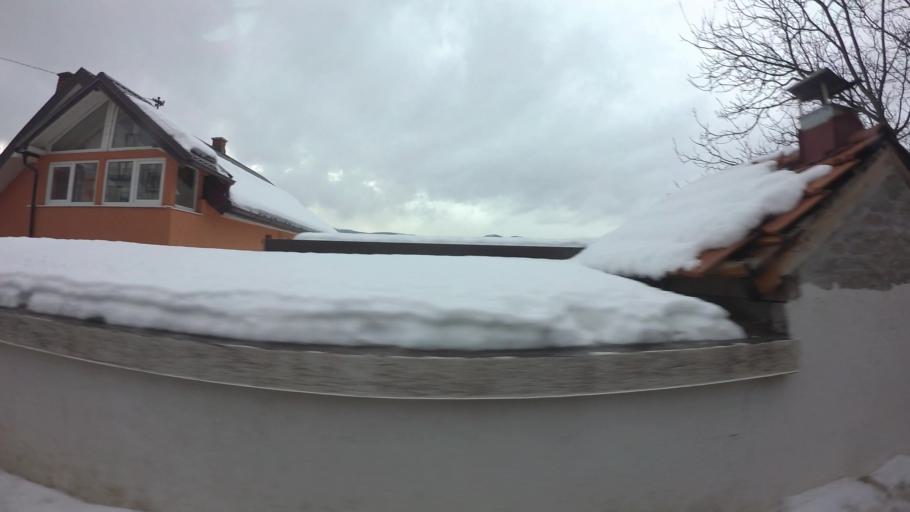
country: BA
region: Federation of Bosnia and Herzegovina
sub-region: Kanton Sarajevo
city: Sarajevo
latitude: 43.8573
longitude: 18.3326
